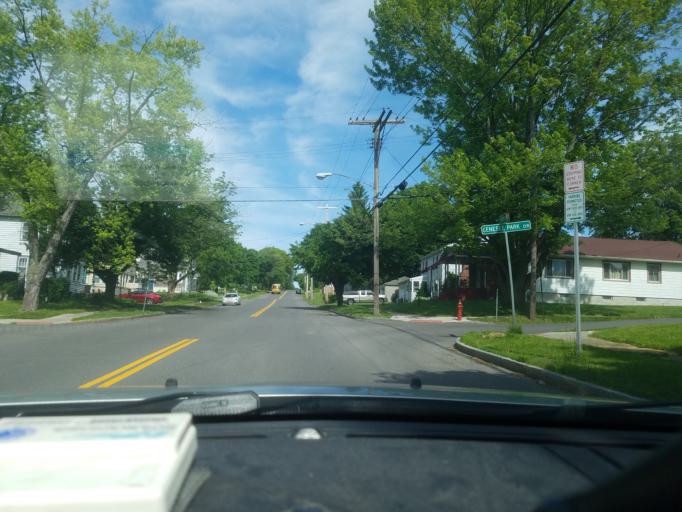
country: US
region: New York
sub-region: Onondaga County
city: East Syracuse
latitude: 43.0483
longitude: -76.1095
